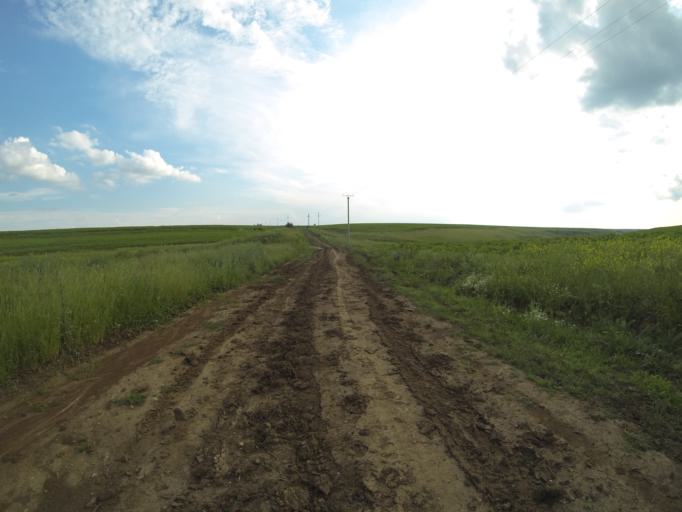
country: RO
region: Dolj
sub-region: Comuna Caloparu
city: Salcuta
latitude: 44.1491
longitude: 23.7011
